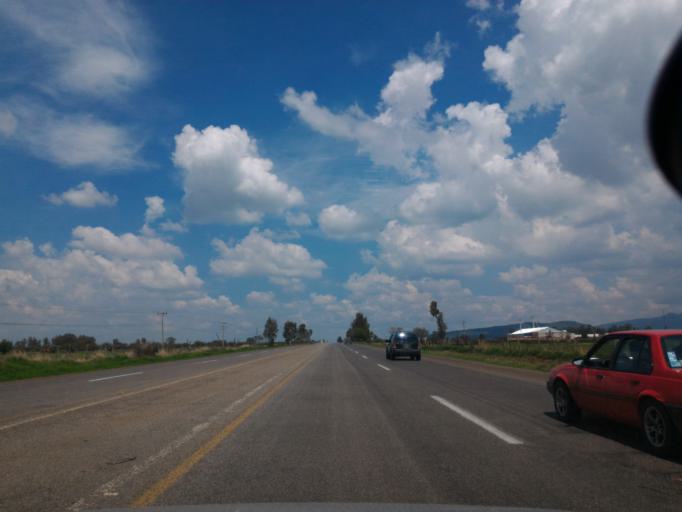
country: MX
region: Jalisco
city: Tepatitlan de Morelos
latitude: 20.8783
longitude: -102.6869
